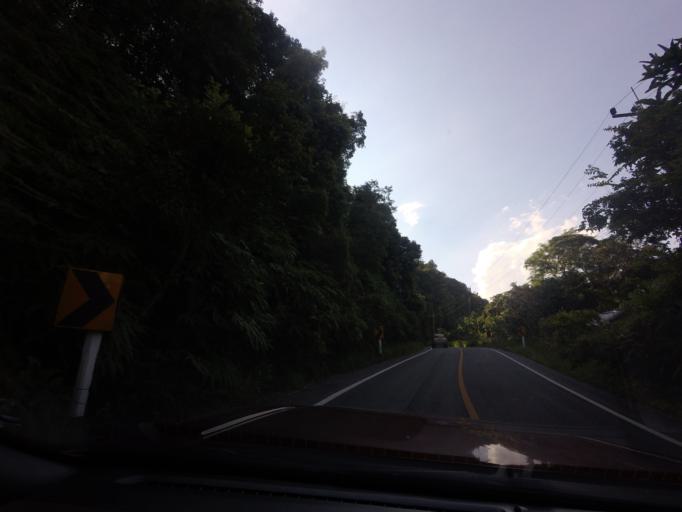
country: TH
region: Yala
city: Than To
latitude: 6.0724
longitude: 101.3365
